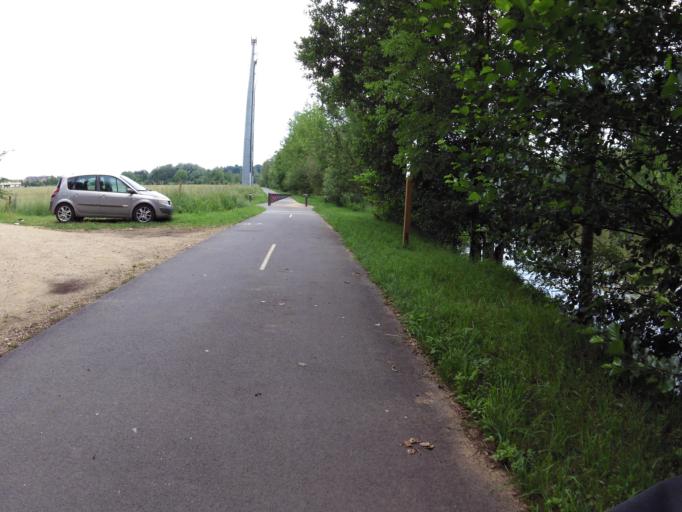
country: FR
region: Champagne-Ardenne
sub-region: Departement des Ardennes
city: Floing
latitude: 49.7116
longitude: 4.9243
